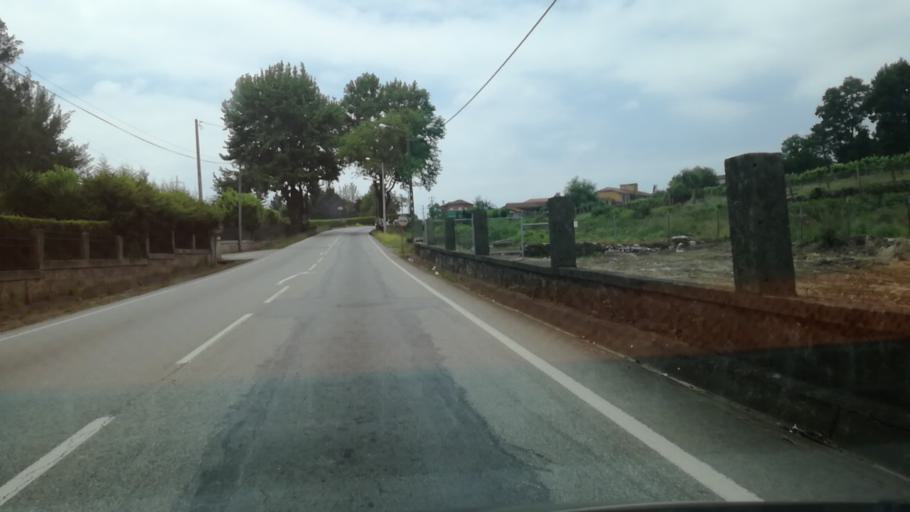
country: PT
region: Porto
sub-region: Maia
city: Anta
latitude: 41.2888
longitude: -8.6016
